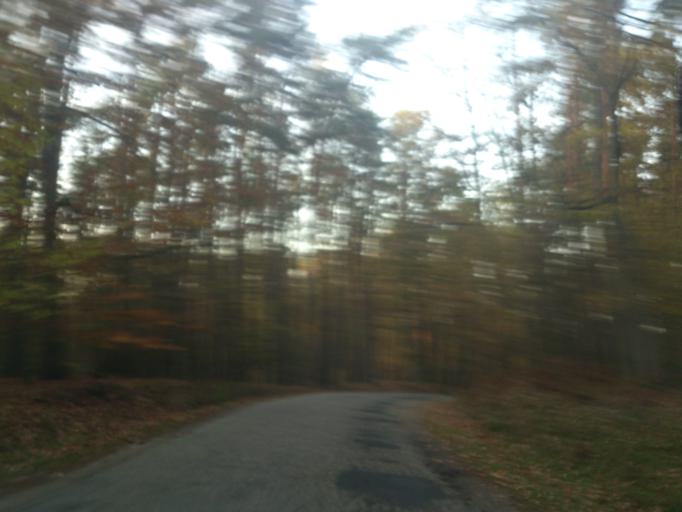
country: PL
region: Kujawsko-Pomorskie
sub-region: Powiat golubsko-dobrzynski
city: Ciechocin
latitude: 53.0862
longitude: 18.9434
